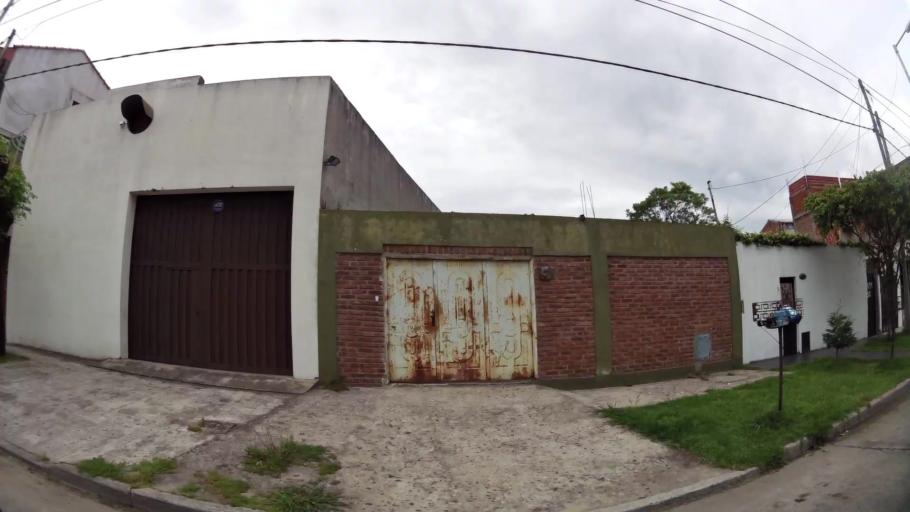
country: AR
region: Buenos Aires
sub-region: Partido de Avellaneda
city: Avellaneda
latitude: -34.6792
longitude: -58.3782
